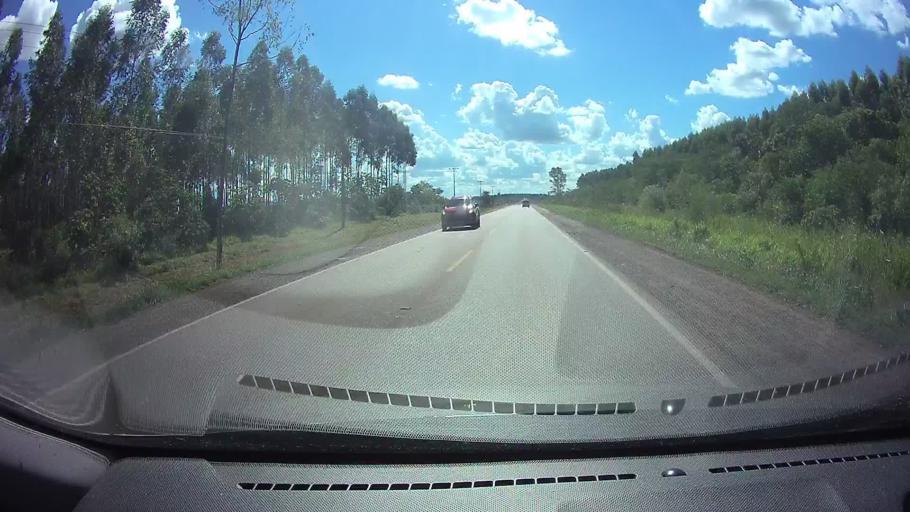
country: PY
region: Guaira
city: Coronel Martinez
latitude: -25.7643
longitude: -56.6824
